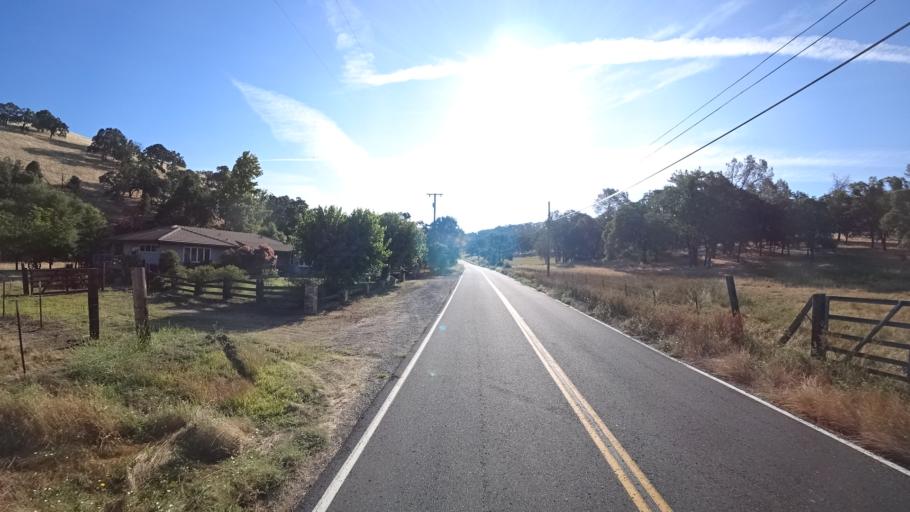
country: US
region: California
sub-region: Calaveras County
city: Valley Springs
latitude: 38.2104
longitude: -120.7811
